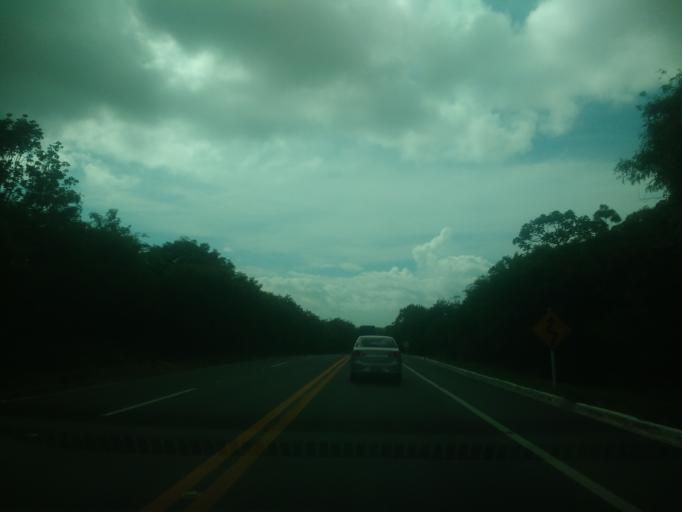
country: BR
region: Alagoas
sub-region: Marechal Deodoro
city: Marechal Deodoro
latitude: -9.6882
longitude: -35.8186
